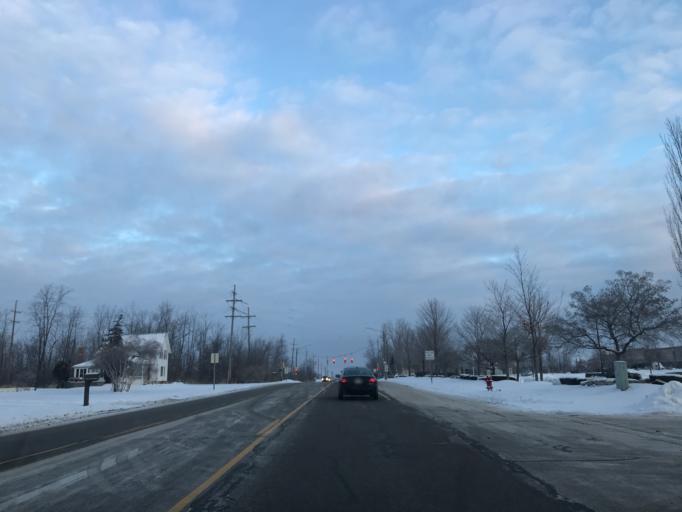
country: US
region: Michigan
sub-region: Oakland County
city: Wixom
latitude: 42.4880
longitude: -83.5353
